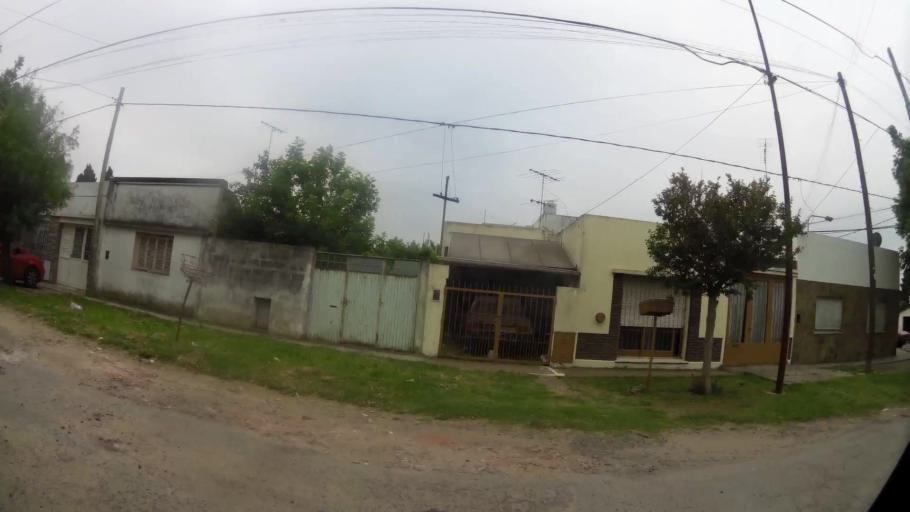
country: AR
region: Buenos Aires
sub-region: Partido de La Plata
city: La Plata
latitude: -34.9254
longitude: -57.9941
